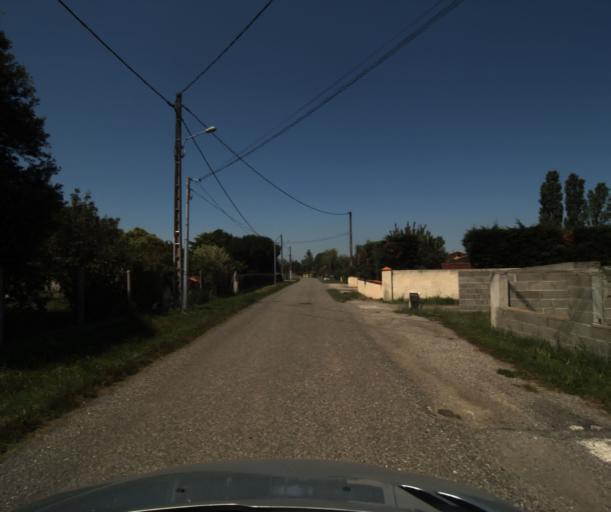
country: FR
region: Midi-Pyrenees
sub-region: Departement de la Haute-Garonne
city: Muret
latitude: 43.4647
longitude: 1.3651
